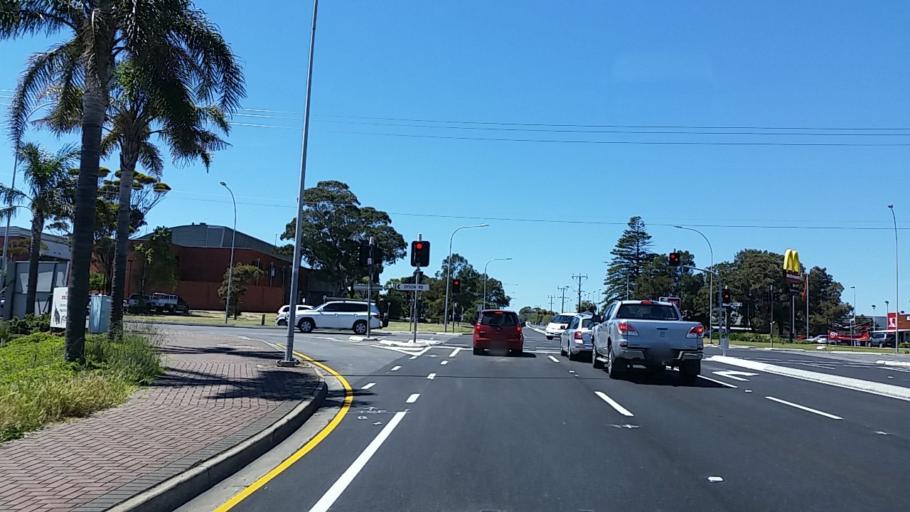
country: AU
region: South Australia
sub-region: Adelaide
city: Port Noarlunga
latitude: -35.1386
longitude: 138.4857
